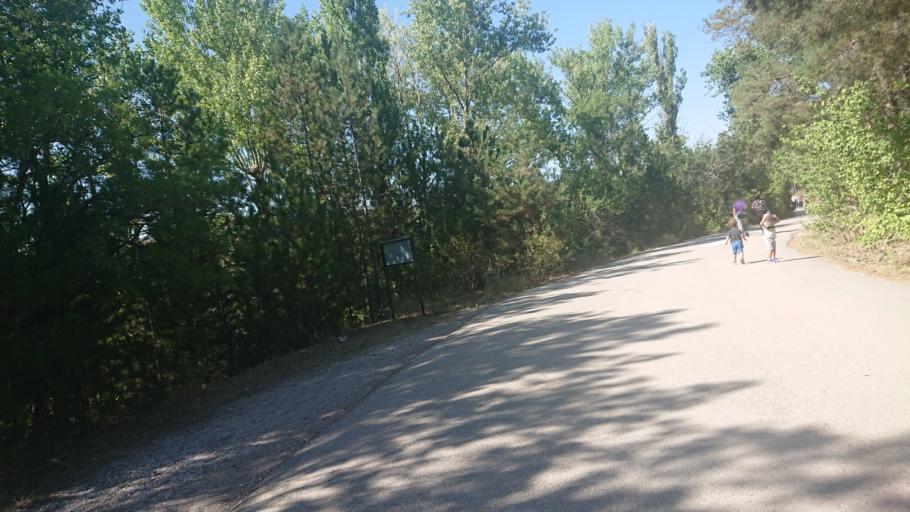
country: TR
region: Ankara
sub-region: Goelbasi
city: Golbasi
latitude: 39.8153
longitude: 32.8212
